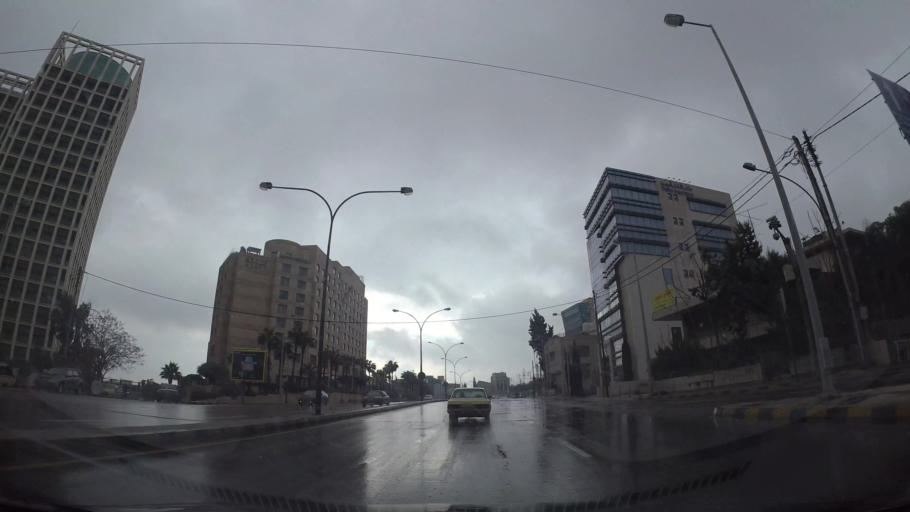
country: JO
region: Amman
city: Amman
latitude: 31.9563
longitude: 35.9083
